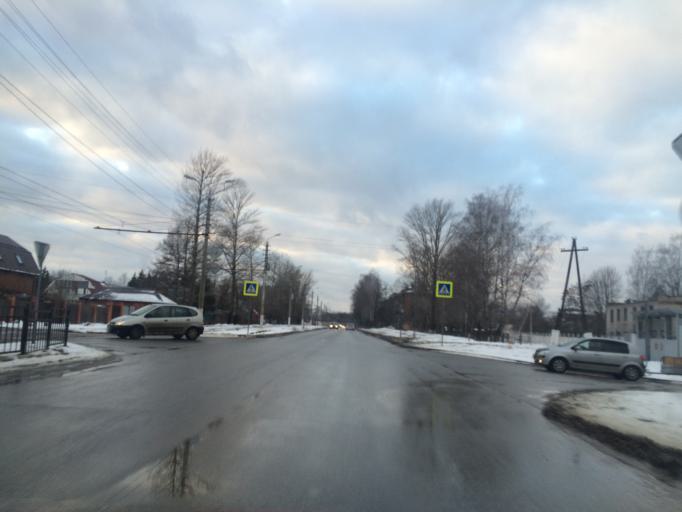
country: RU
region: Tula
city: Tula
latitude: 54.2191
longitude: 37.7044
